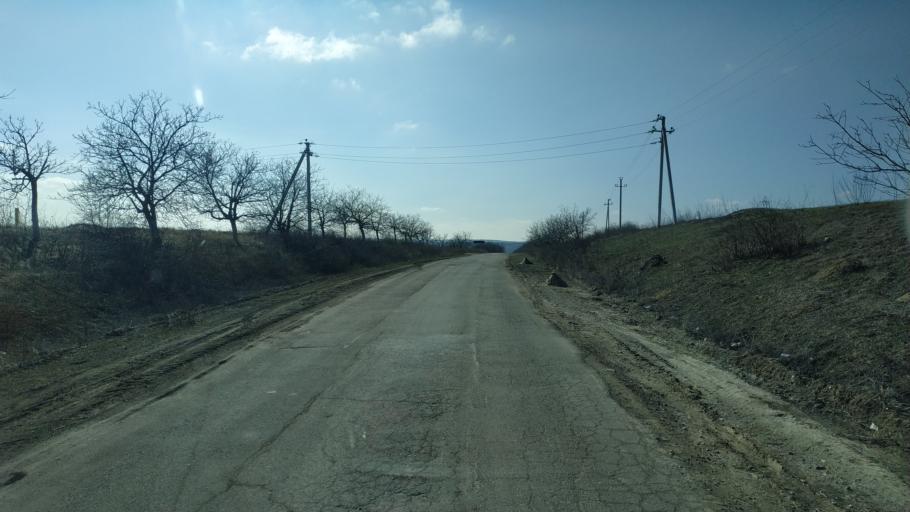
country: MD
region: Hincesti
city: Hincesti
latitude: 46.7647
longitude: 28.6738
